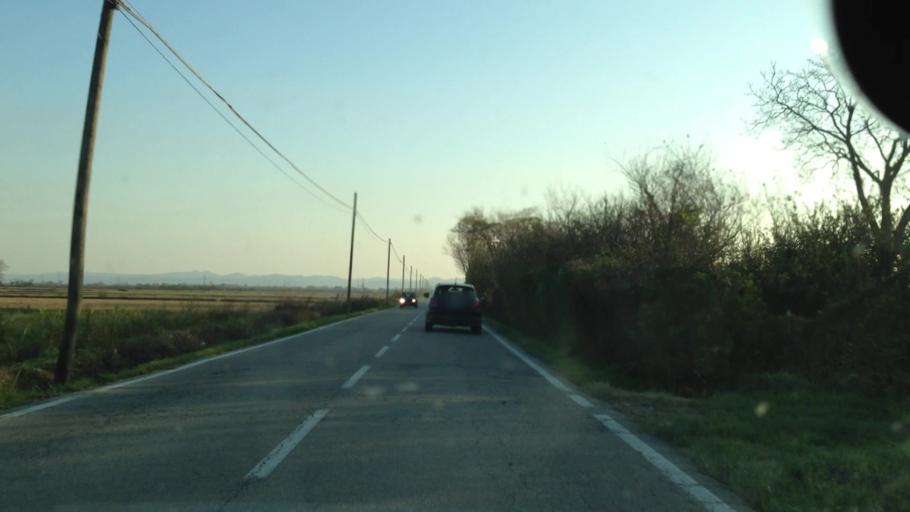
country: IT
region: Piedmont
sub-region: Provincia di Vercelli
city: Livorno Ferraris
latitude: 45.2664
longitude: 8.0829
